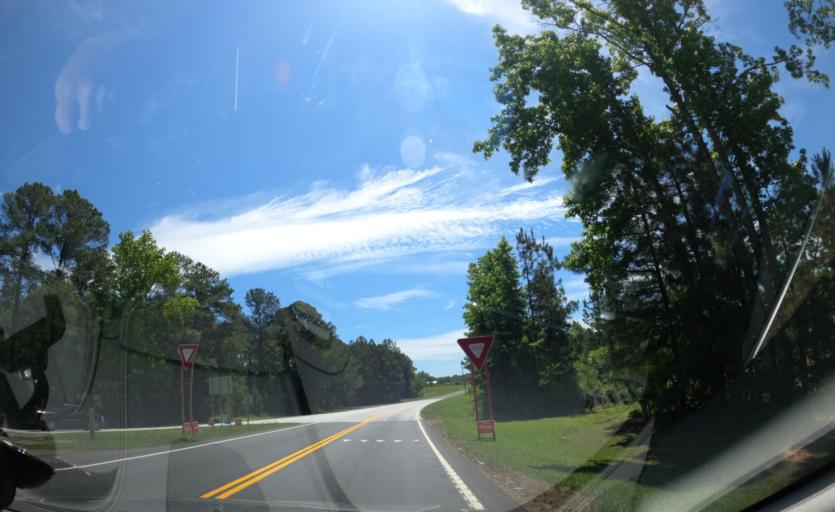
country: US
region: South Carolina
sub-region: McCormick County
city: McCormick
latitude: 33.9267
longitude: -82.3179
